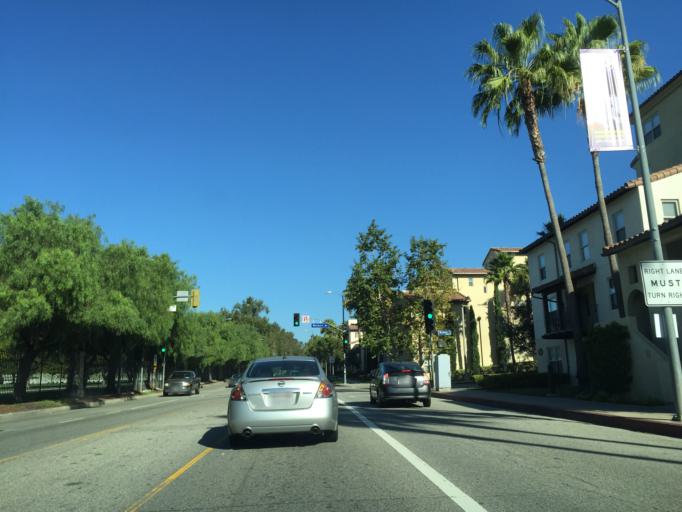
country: US
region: California
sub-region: Los Angeles County
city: Westwood, Los Angeles
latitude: 34.0611
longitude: -118.4504
